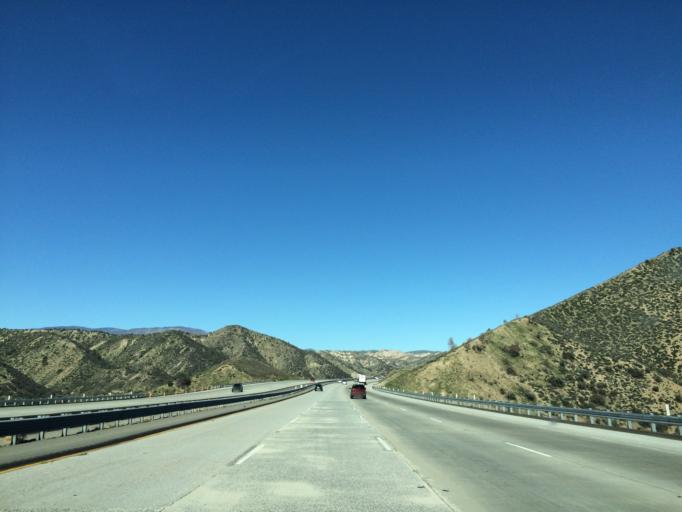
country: US
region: California
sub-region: Kern County
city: Lebec
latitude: 34.6866
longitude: -118.7852
